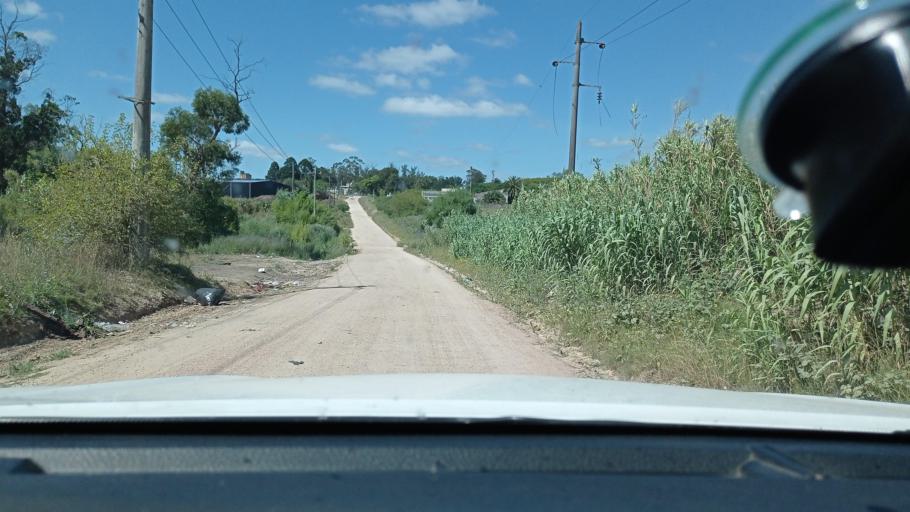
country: UY
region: Canelones
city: Pando
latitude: -34.7295
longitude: -55.9748
